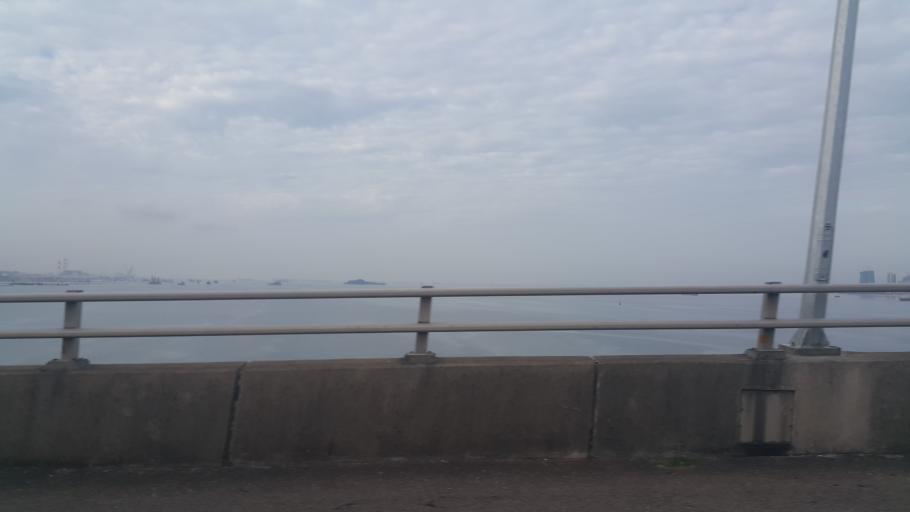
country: MY
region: Johor
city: Johor Bahru
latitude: 1.3514
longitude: 103.6322
